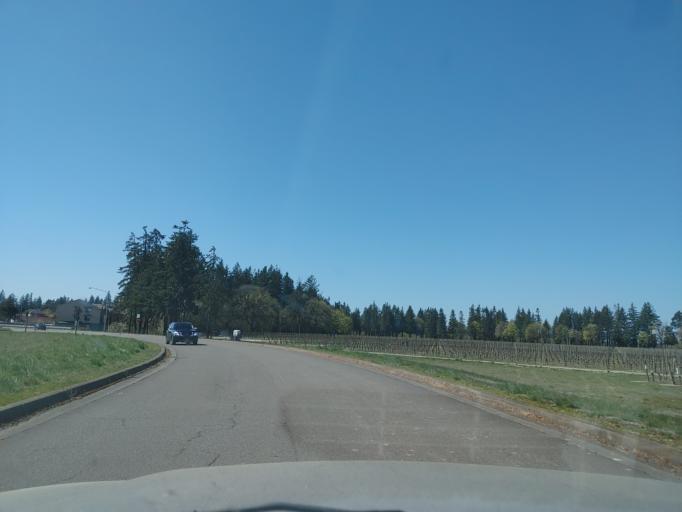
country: US
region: Oregon
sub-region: Yamhill County
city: McMinnville
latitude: 45.2019
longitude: -123.1510
